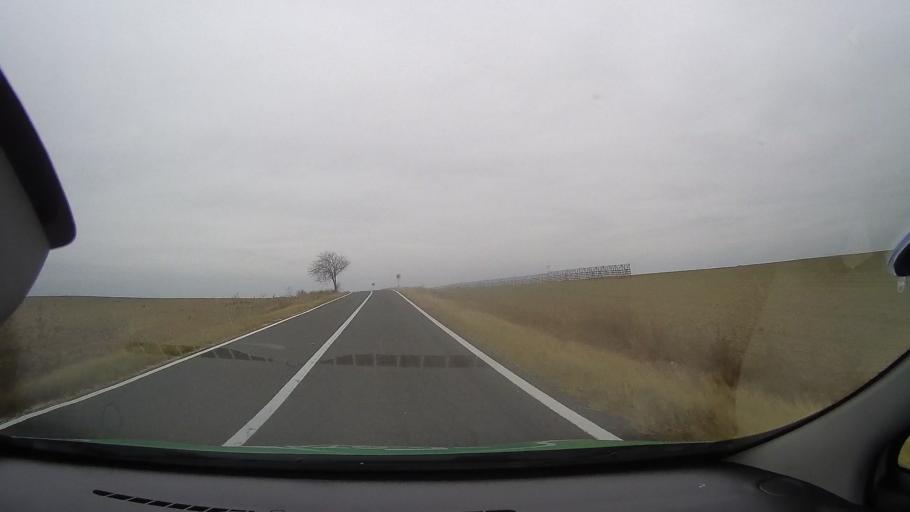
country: RO
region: Constanta
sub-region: Comuna Saraiu
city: Saraiu
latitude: 44.7108
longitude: 28.1073
